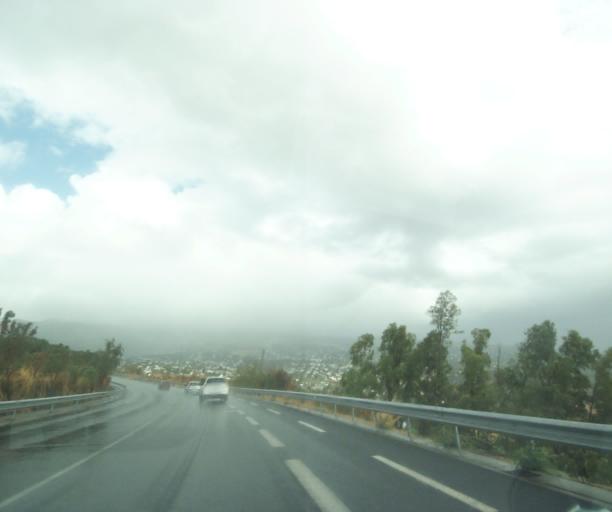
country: RE
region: Reunion
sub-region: Reunion
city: Le Port
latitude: -20.9730
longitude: 55.3142
